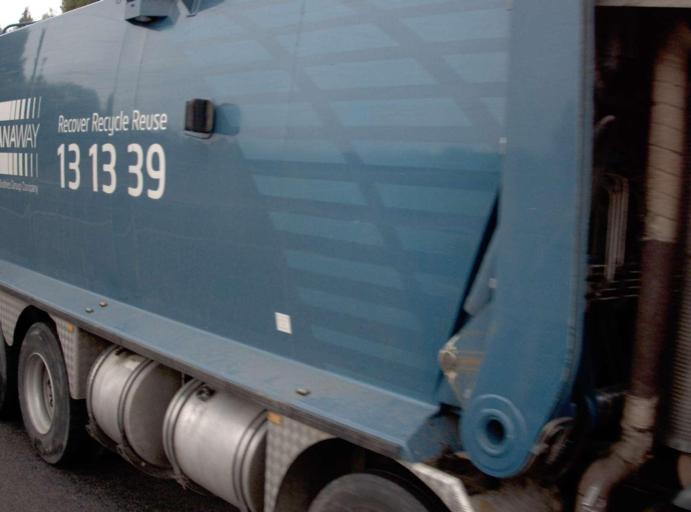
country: AU
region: Victoria
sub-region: Latrobe
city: Morwell
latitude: -38.2921
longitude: 146.4155
